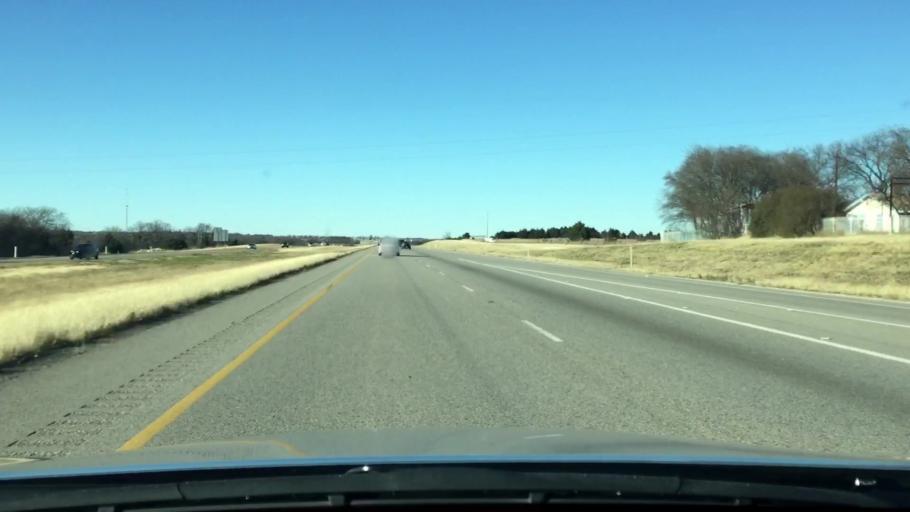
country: US
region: Texas
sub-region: Johnson County
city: Grandview
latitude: 32.2337
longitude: -97.1551
